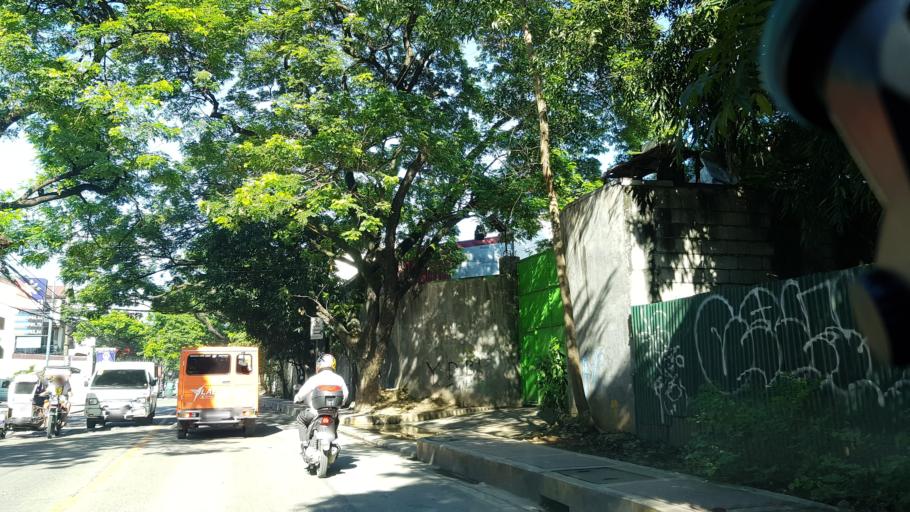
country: PH
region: Calabarzon
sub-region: Province of Rizal
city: Cainta
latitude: 14.5755
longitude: 121.0964
